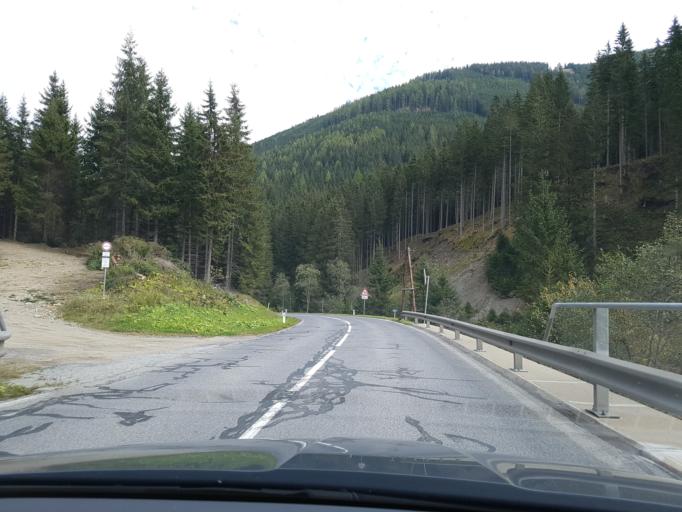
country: AT
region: Salzburg
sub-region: Politischer Bezirk Tamsweg
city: Ramingstein
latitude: 46.9774
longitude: 13.8997
